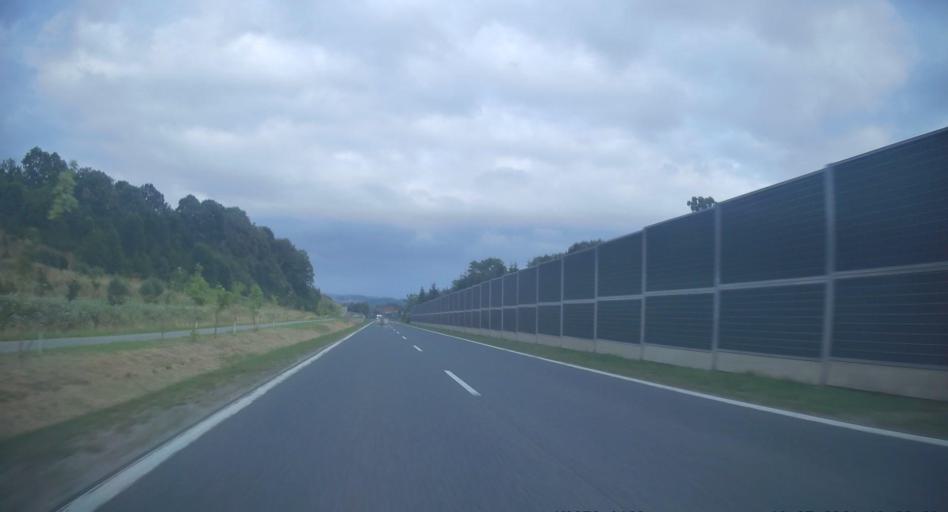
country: PL
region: Lower Silesian Voivodeship
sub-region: Powiat klodzki
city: Jugow
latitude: 50.6118
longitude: 16.4922
